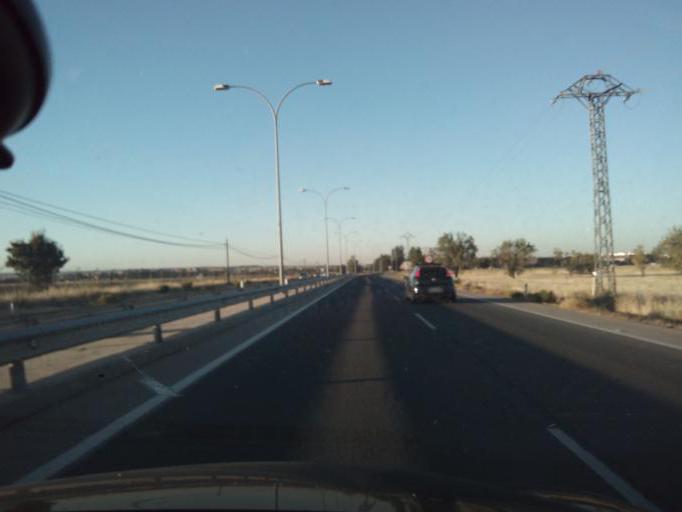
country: ES
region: Madrid
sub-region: Provincia de Madrid
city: Torrejon de Ardoz
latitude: 40.4830
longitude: -3.4779
